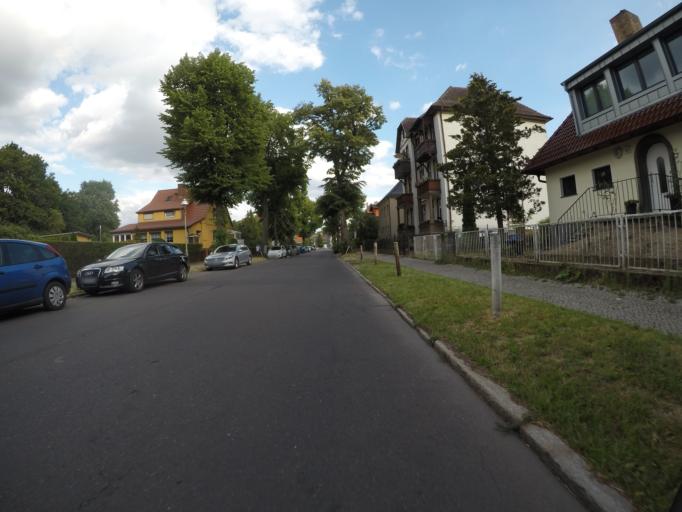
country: DE
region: Berlin
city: Kaulsdorf
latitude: 52.5090
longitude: 13.5900
